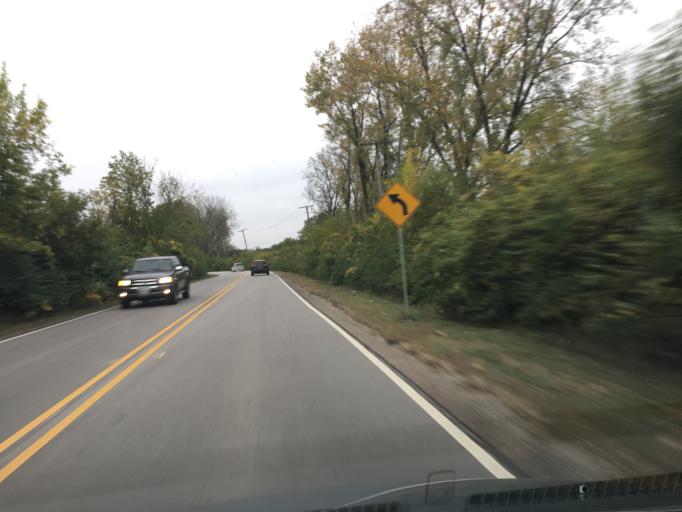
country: US
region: Illinois
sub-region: Will County
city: Plainfield
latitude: 41.6361
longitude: -88.1664
